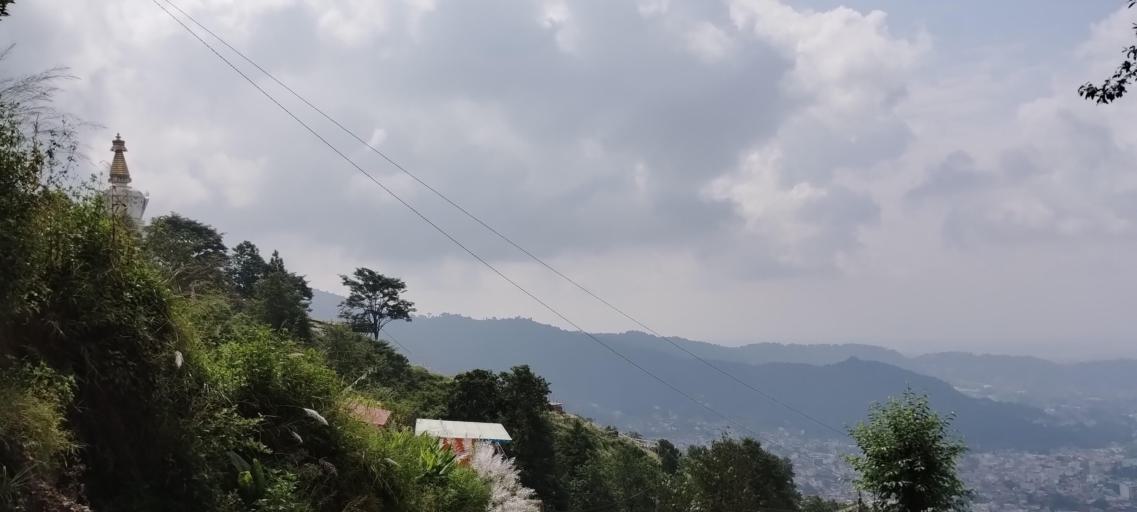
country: NP
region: Central Region
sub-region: Bagmati Zone
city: Kathmandu
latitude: 27.7917
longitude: 85.3590
